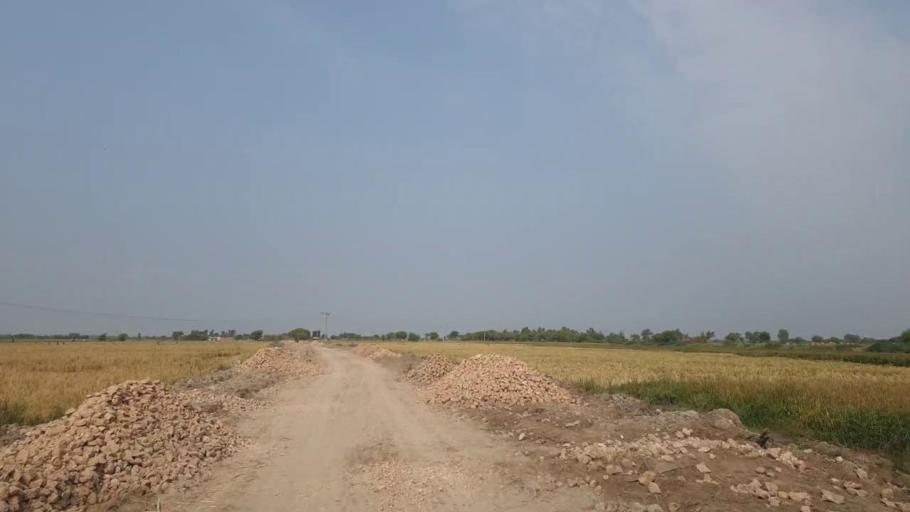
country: PK
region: Sindh
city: Badin
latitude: 24.6114
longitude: 68.7415
